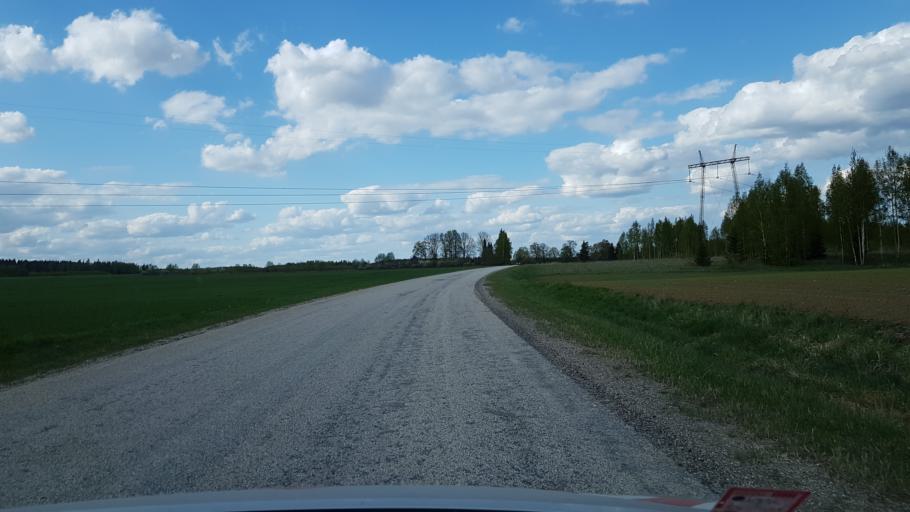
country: EE
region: Tartu
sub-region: UElenurme vald
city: Ulenurme
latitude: 58.2734
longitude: 26.9072
